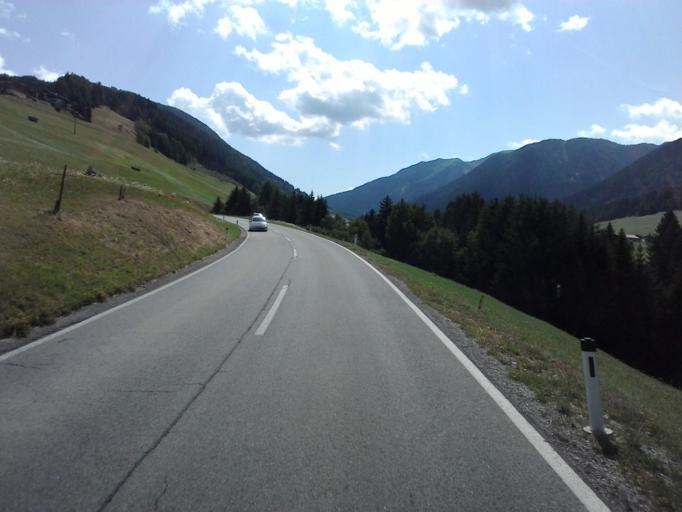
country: AT
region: Tyrol
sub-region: Politischer Bezirk Lienz
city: Strassen
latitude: 46.7366
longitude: 12.4740
